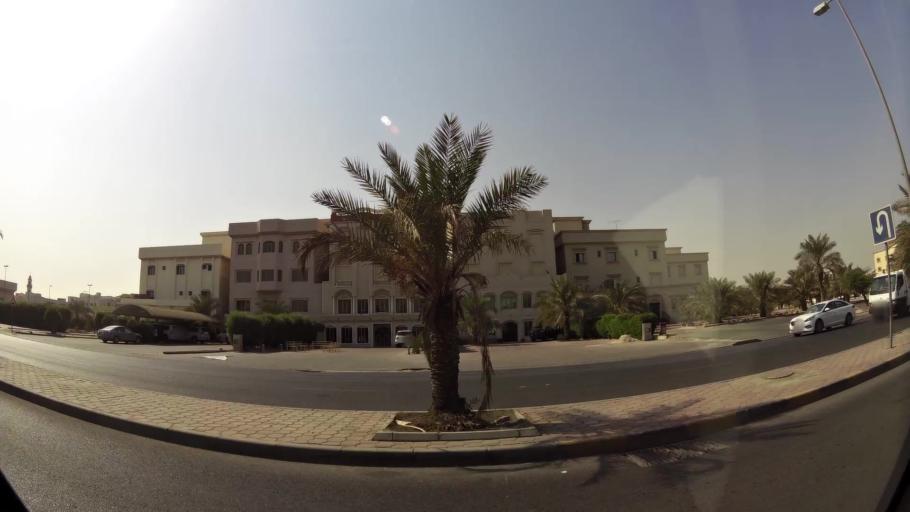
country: KW
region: Al Ahmadi
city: Al Fahahil
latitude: 29.0901
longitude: 48.1228
